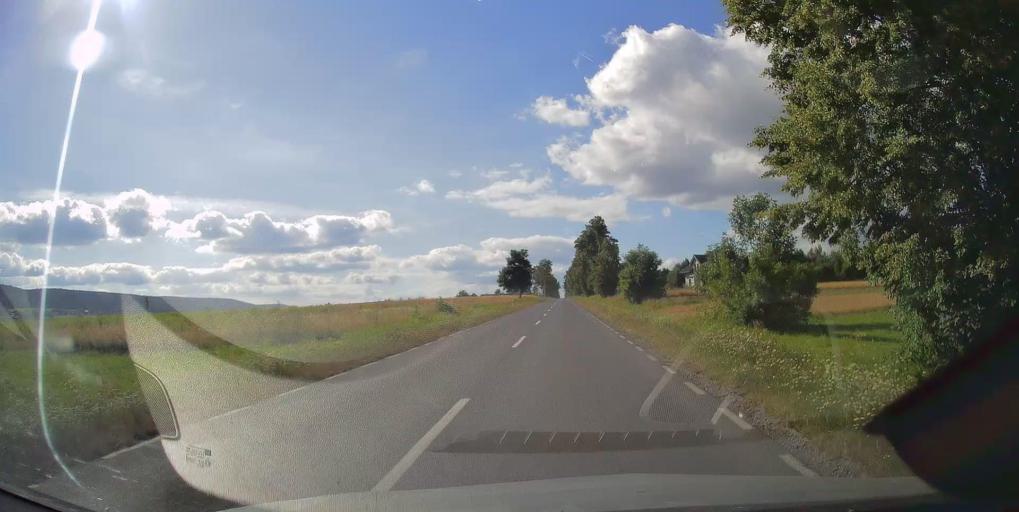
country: PL
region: Swietokrzyskie
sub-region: Powiat kielecki
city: Bodzentyn
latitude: 50.9547
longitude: 20.9180
